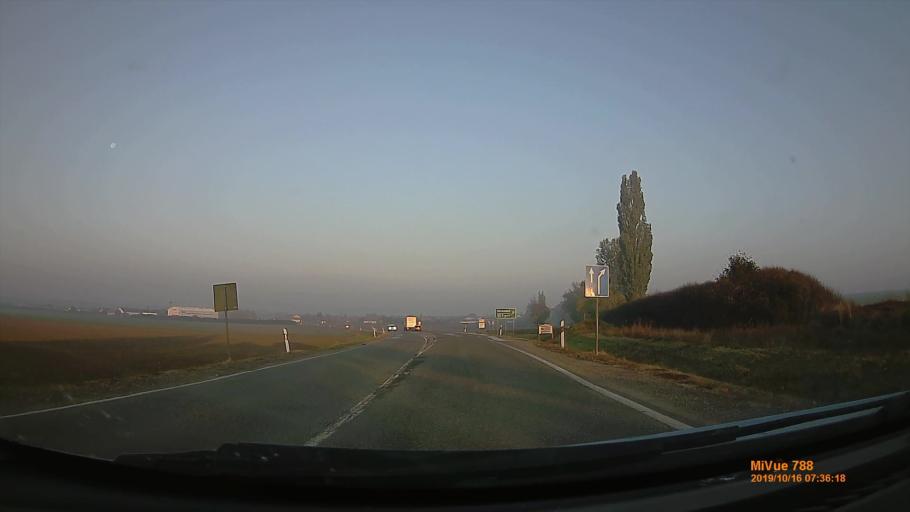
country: HU
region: Heves
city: Kerecsend
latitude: 47.7855
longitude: 20.3597
